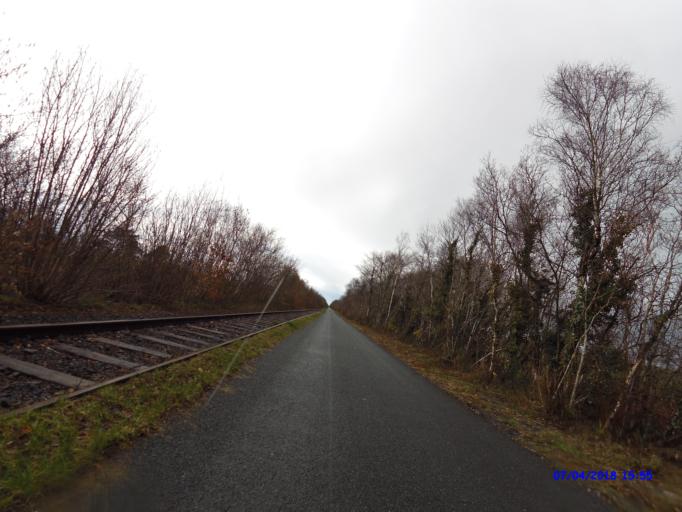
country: IE
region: Leinster
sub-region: An Iarmhi
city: Athlone
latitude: 53.4175
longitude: -7.8728
